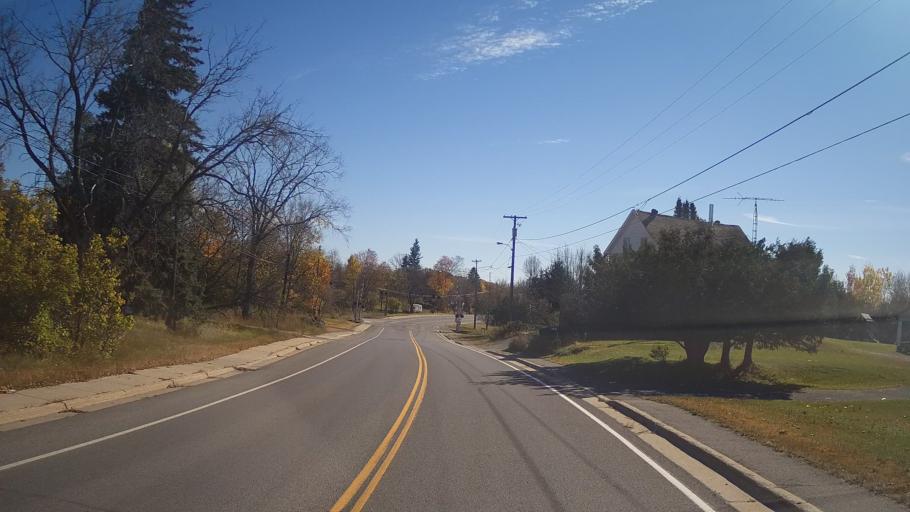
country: CA
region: Ontario
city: Kingston
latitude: 44.6665
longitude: -76.6772
